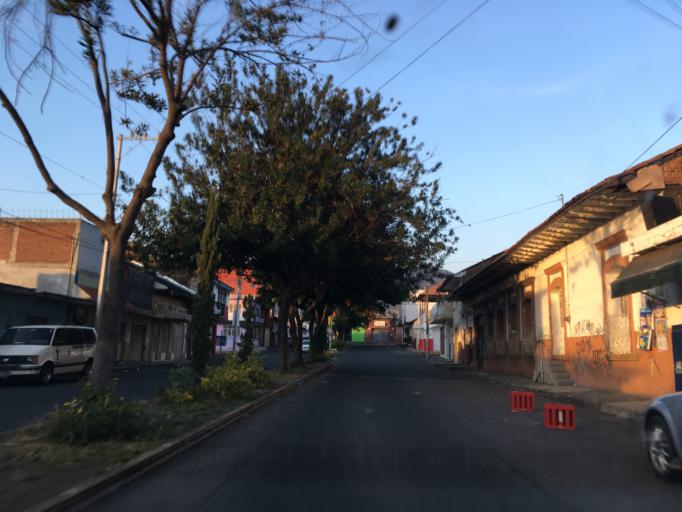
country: MX
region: Michoacan
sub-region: Uruapan
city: Uruapan
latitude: 19.4162
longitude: -102.0586
